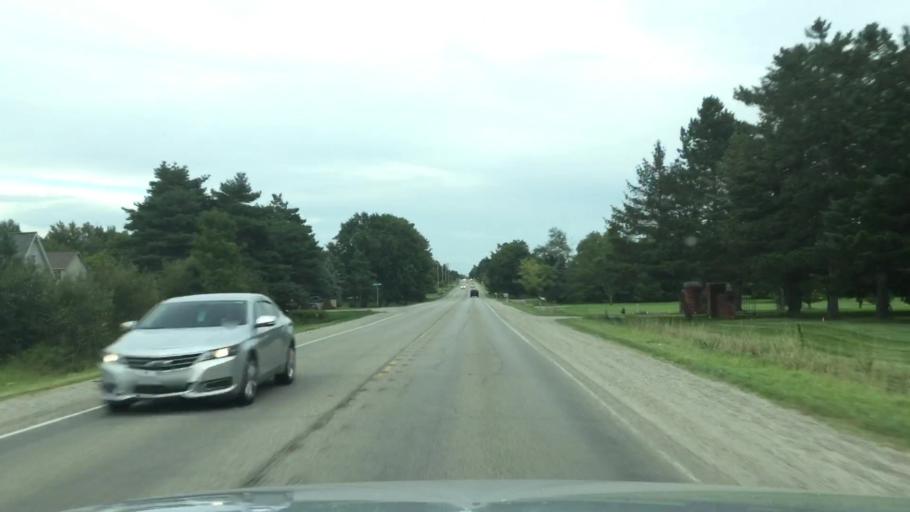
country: US
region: Michigan
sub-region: Genesee County
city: Lake Fenton
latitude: 42.8861
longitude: -83.6685
